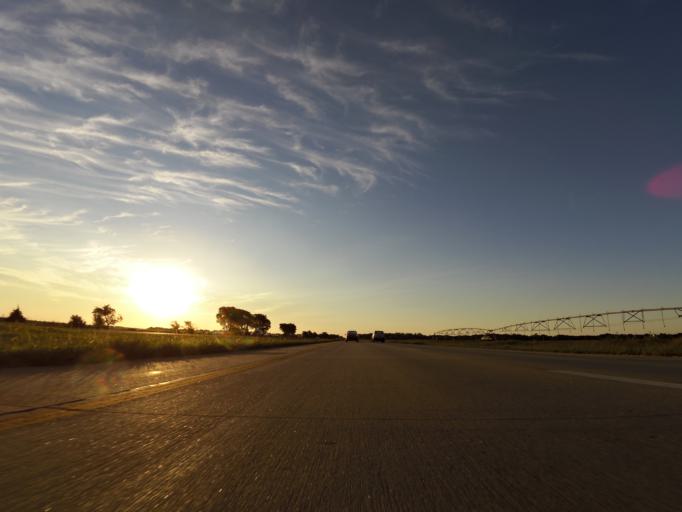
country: US
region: Kansas
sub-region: Reno County
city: Haven
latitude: 37.8881
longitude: -97.7441
